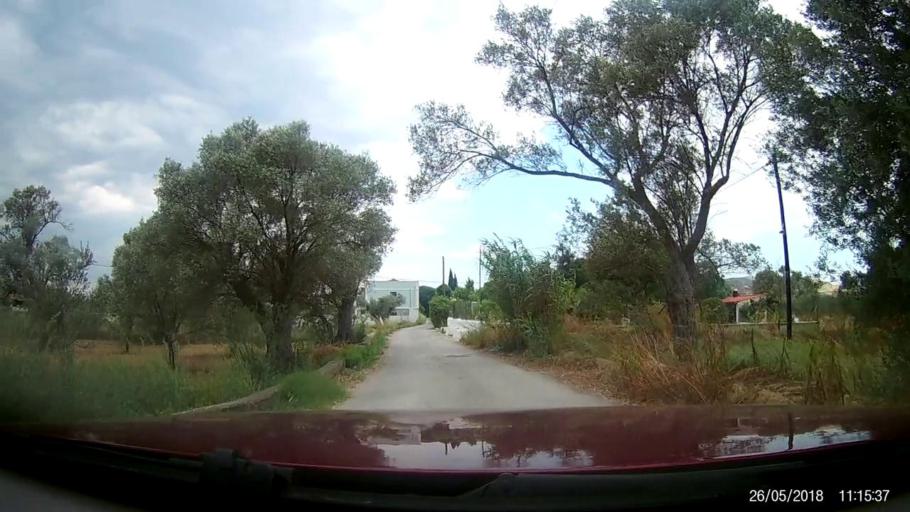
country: GR
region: Central Greece
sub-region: Nomos Evvoias
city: Mytikas
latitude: 38.4462
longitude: 23.6557
